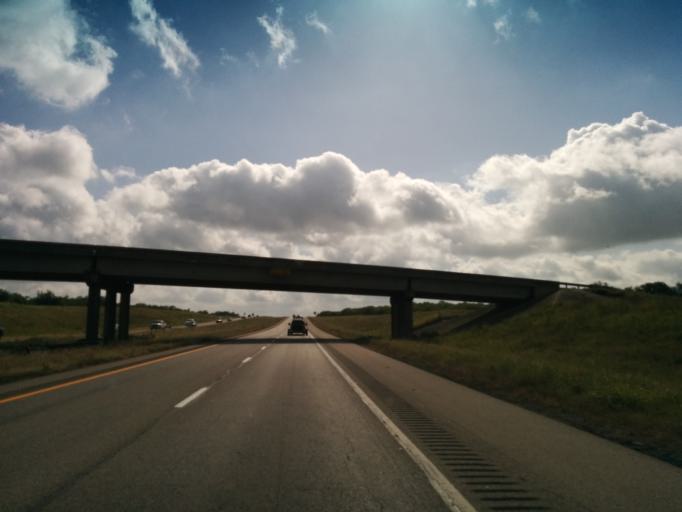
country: US
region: Texas
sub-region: Caldwell County
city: Luling
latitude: 29.6447
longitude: -97.6981
